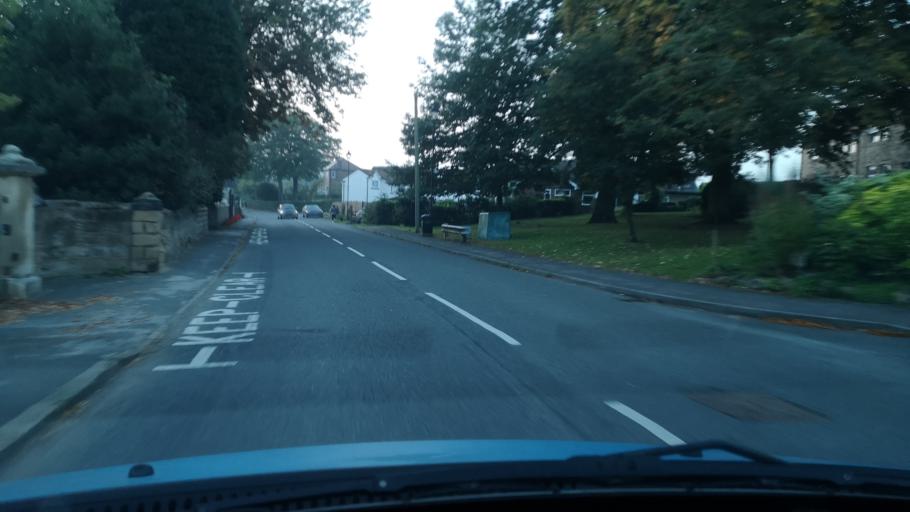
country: GB
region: England
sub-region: City and Borough of Wakefield
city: Badsworth
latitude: 53.6279
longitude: -1.2990
